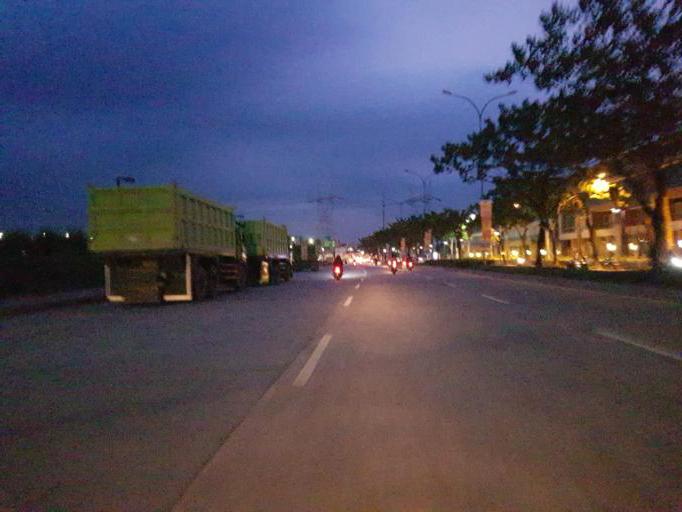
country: ID
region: West Java
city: Serpong
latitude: -6.3181
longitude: 106.6465
